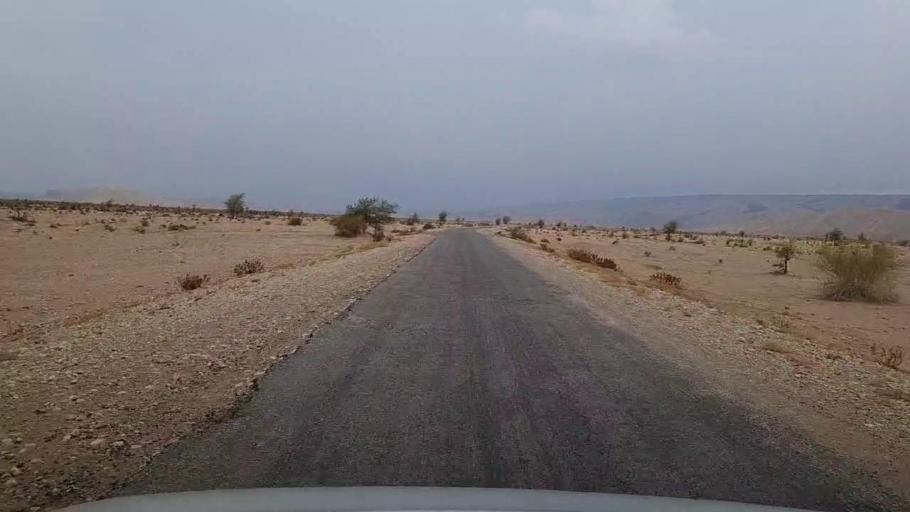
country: PK
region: Sindh
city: Sehwan
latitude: 26.2629
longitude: 67.7229
